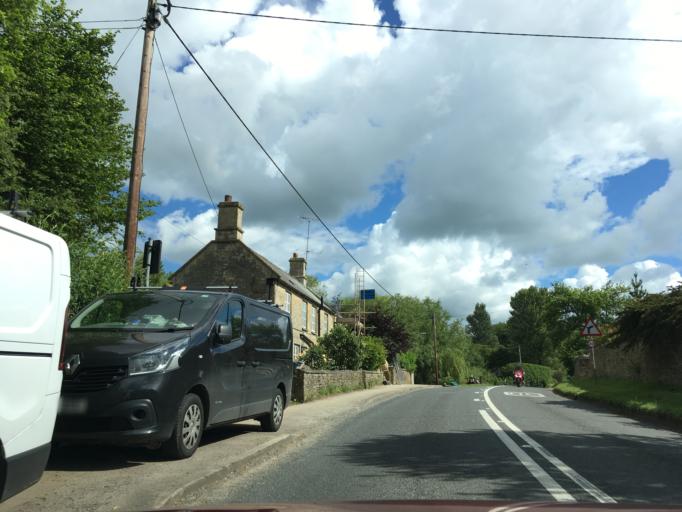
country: GB
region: England
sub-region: Oxfordshire
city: Burford
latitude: 51.8158
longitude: -1.6248
